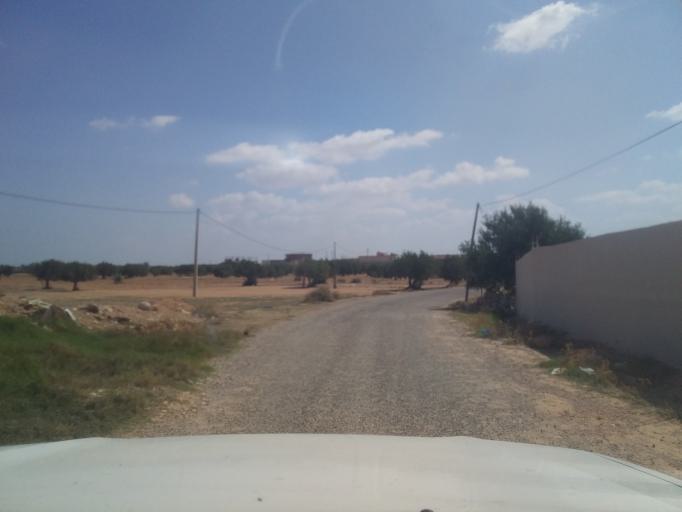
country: TN
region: Madanin
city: Medenine
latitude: 33.6115
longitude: 10.3076
